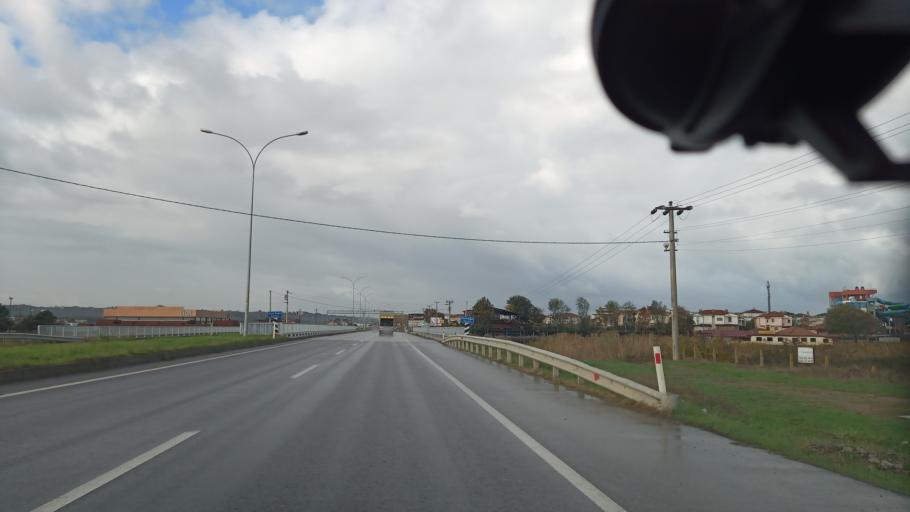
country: TR
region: Sakarya
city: Karasu
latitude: 41.0874
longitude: 30.7460
